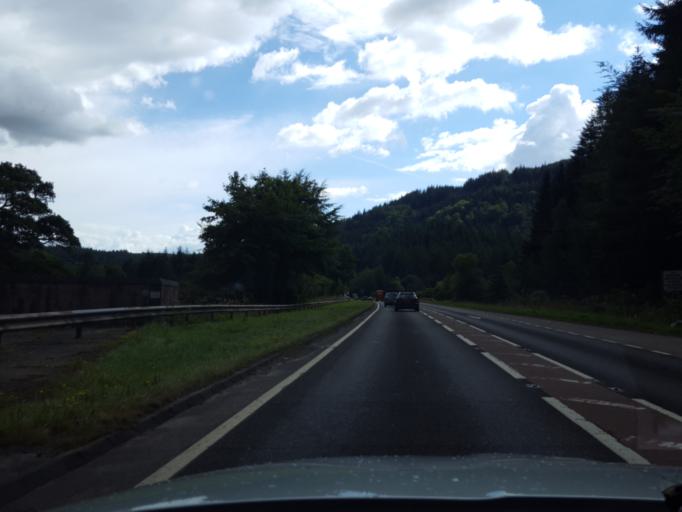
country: GB
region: Scotland
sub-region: Perth and Kinross
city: Bankfoot
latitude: 56.5742
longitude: -3.6226
